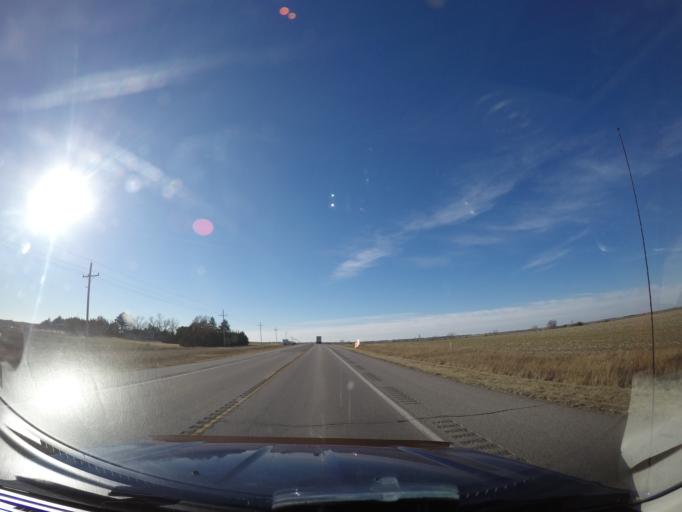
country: US
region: Kansas
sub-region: Marion County
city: Hillsboro
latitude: 38.3626
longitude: -97.2686
